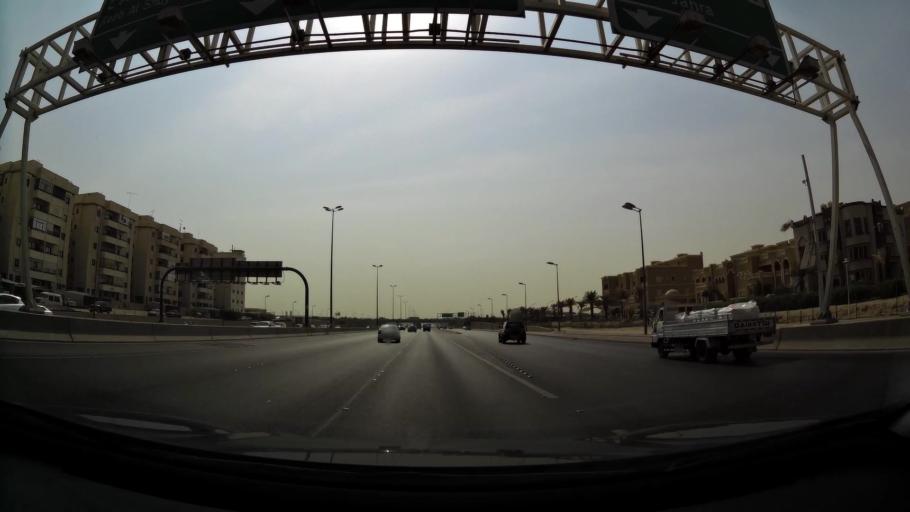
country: KW
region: Al Farwaniyah
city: Al Farwaniyah
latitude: 29.2709
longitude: 47.9511
